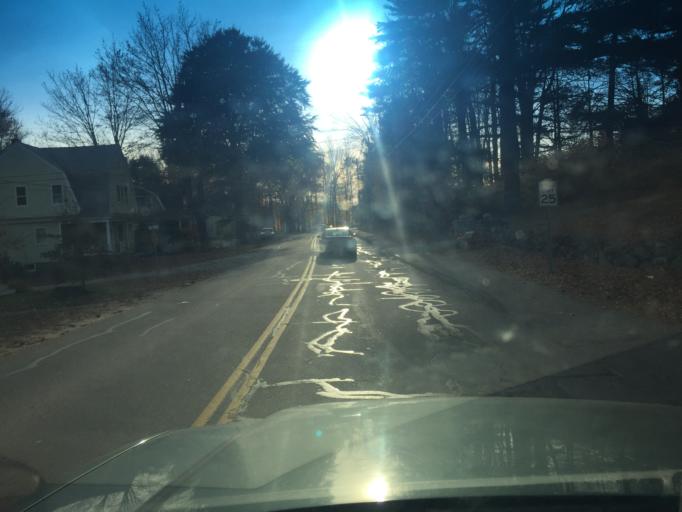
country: US
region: Maine
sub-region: York County
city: York Harbor
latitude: 43.1458
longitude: -70.6468
